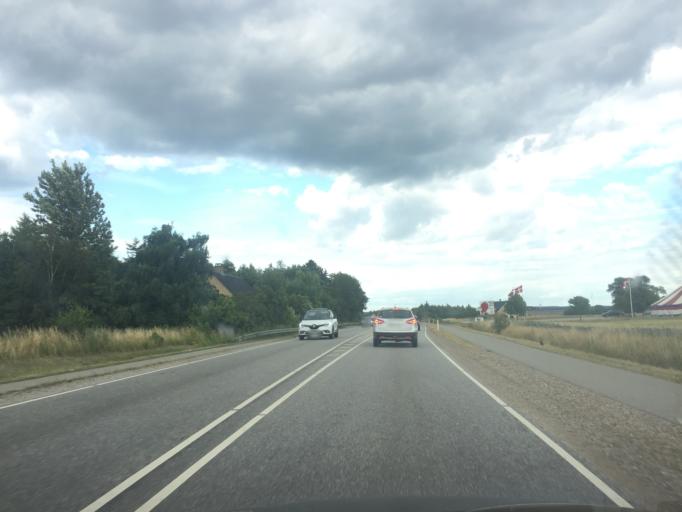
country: DK
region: Capital Region
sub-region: Frederikssund Kommune
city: Slangerup
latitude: 55.8990
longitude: 12.2263
